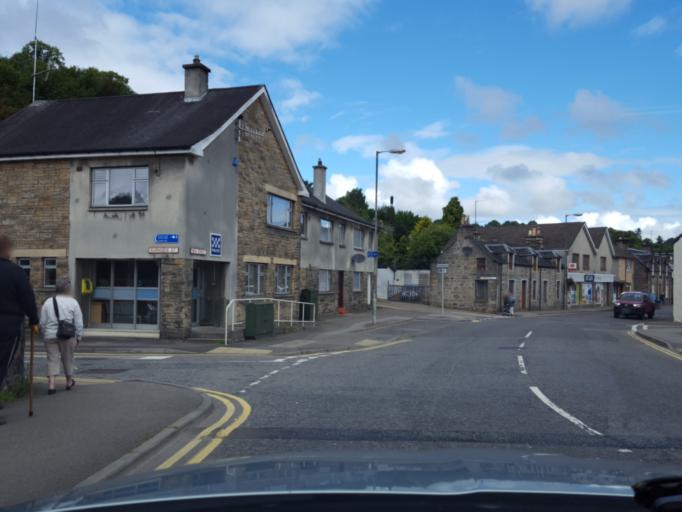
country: GB
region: Scotland
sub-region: Moray
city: Rothes
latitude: 57.5271
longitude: -3.2080
